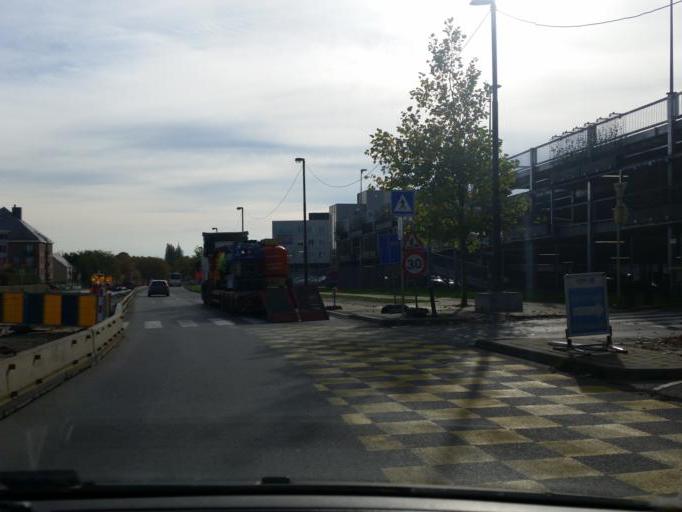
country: BE
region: Flanders
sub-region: Provincie Vlaams-Brabant
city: Wemmel
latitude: 50.8904
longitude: 4.3089
